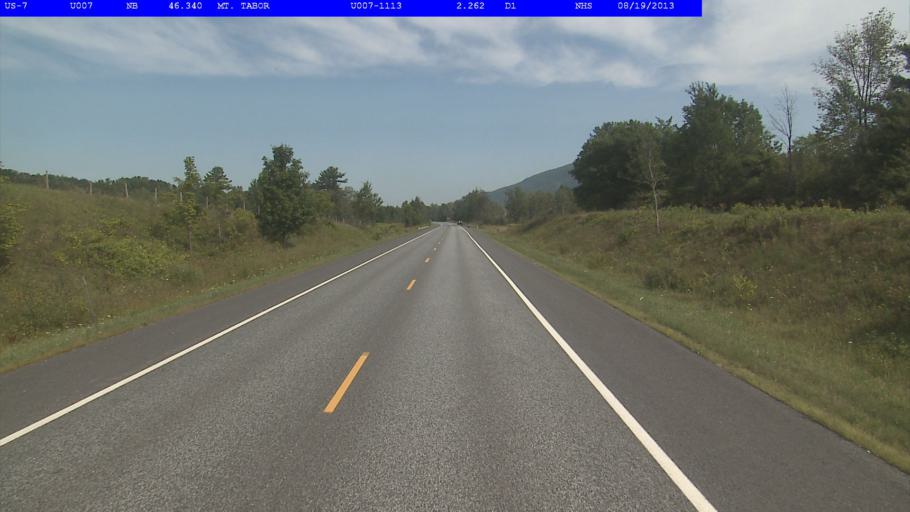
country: US
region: Vermont
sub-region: Bennington County
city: Manchester Center
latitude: 43.3376
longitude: -72.9921
